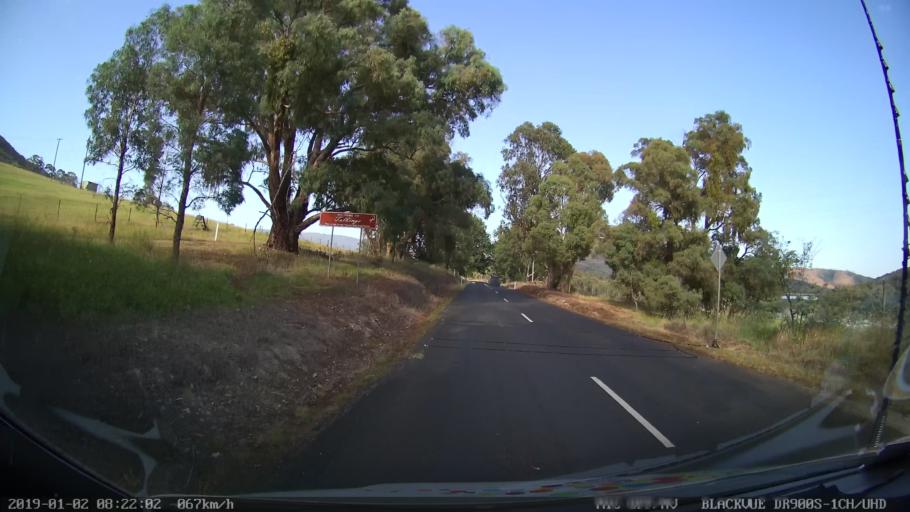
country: AU
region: New South Wales
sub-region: Tumut Shire
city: Tumut
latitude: -35.5694
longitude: 148.3200
